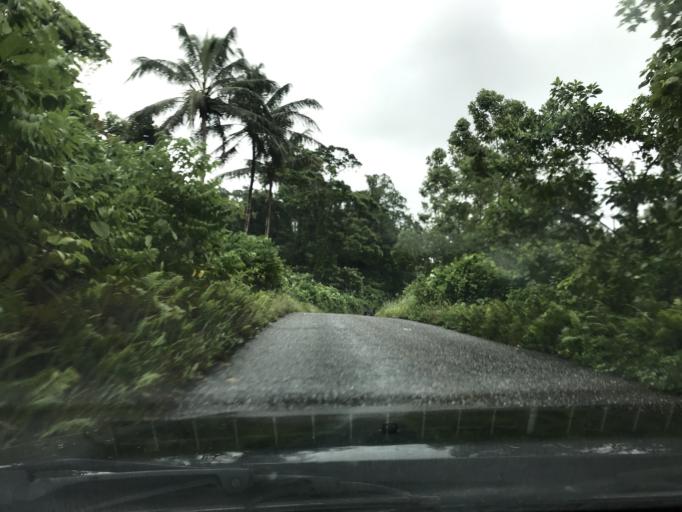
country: SB
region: Western Province
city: Gizo
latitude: -8.2645
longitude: 157.2357
